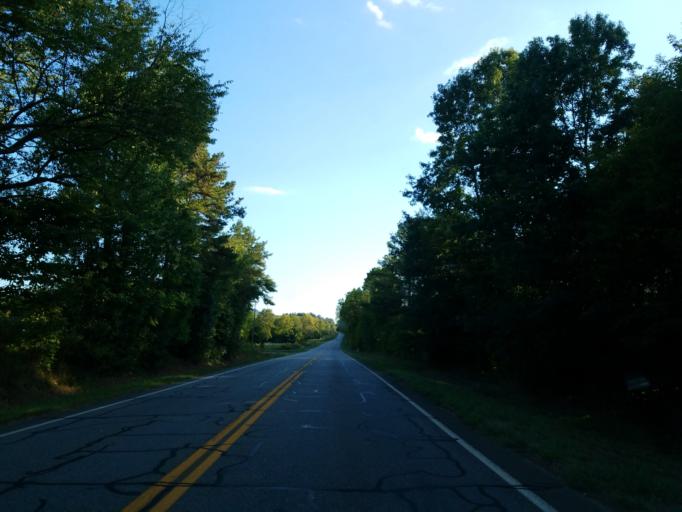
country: US
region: Georgia
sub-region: Murray County
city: Chatsworth
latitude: 34.5578
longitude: -84.7078
